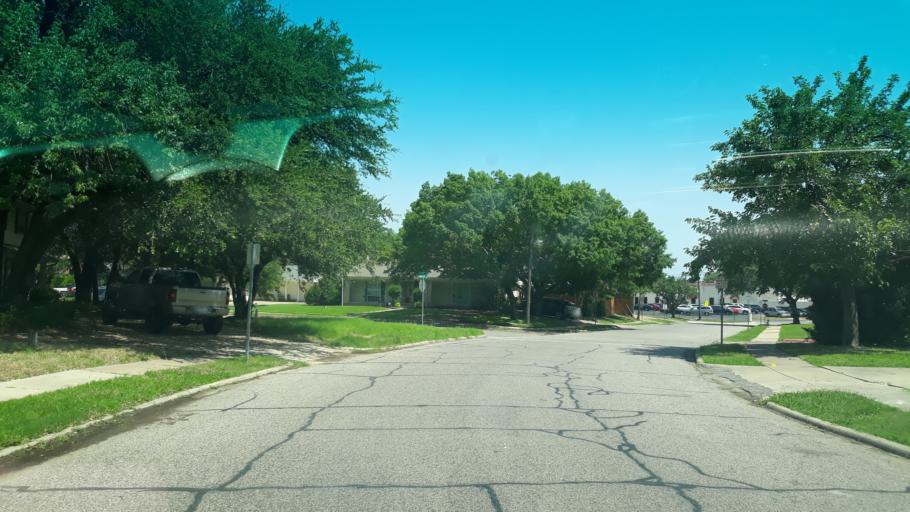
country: US
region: Texas
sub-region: Dallas County
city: Irving
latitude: 32.8545
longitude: -96.9611
